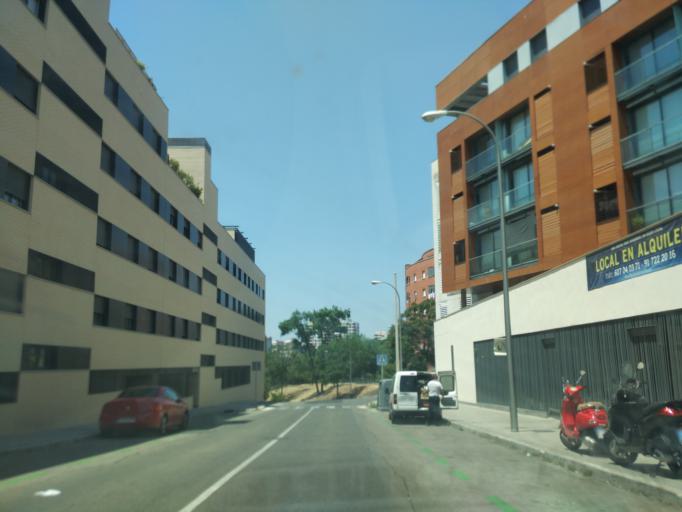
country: ES
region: Madrid
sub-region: Provincia de Madrid
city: Tetuan de las Victorias
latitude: 40.4715
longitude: -3.6962
